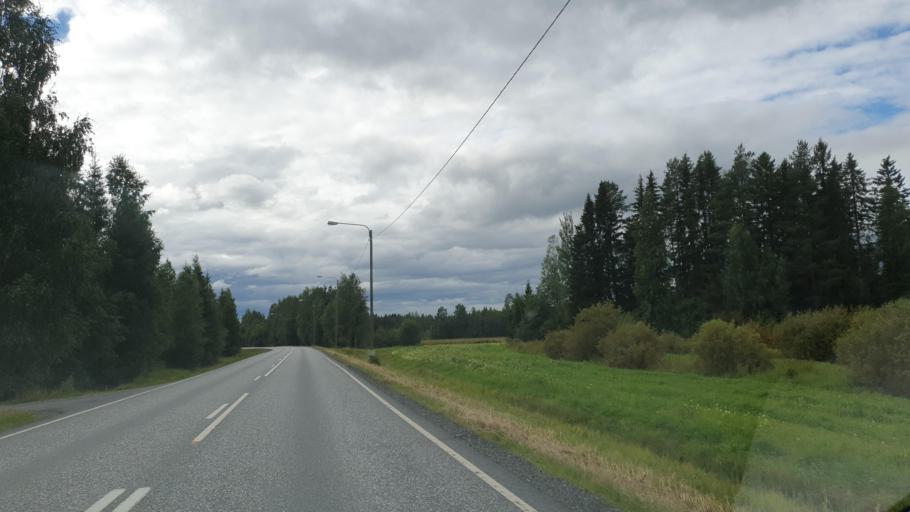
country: FI
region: Northern Savo
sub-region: Ylae-Savo
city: Iisalmi
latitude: 63.5212
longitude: 27.1471
